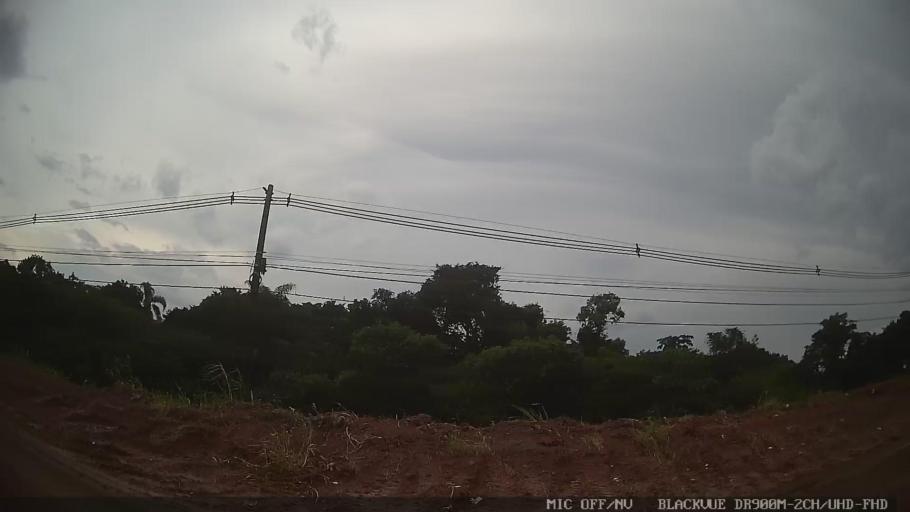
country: BR
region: Sao Paulo
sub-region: Itaquaquecetuba
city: Itaquaquecetuba
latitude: -23.4621
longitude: -46.3024
